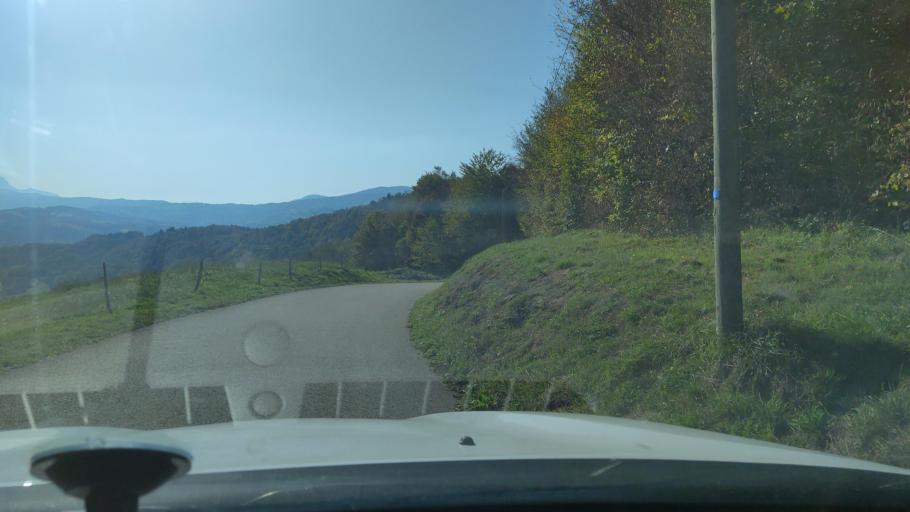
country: FR
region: Rhone-Alpes
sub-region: Departement de la Savoie
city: Les Echelles
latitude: 45.4625
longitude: 5.7792
